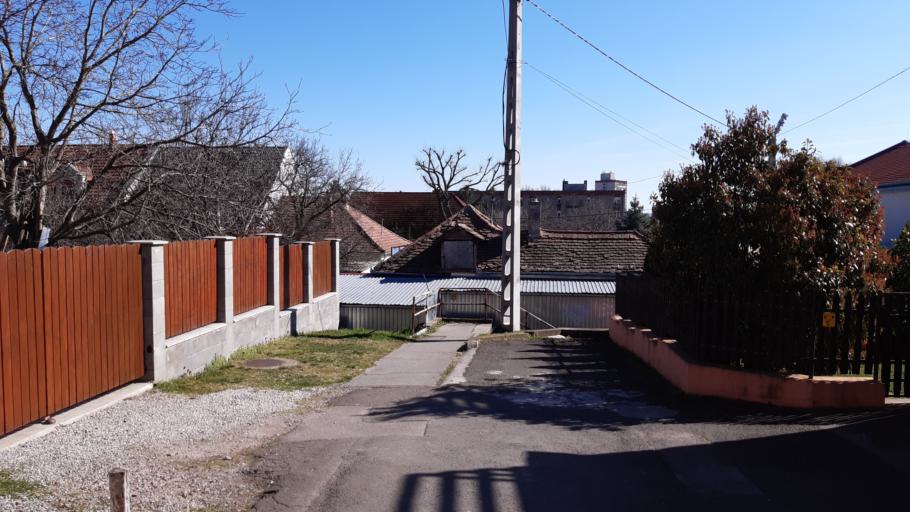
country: HU
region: Baranya
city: Pecs
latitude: 46.0703
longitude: 18.1965
